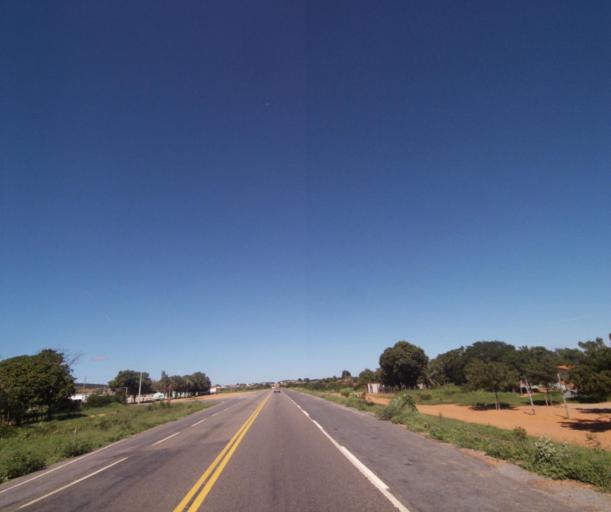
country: BR
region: Bahia
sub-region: Palmas De Monte Alto
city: Palmas de Monte Alto
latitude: -14.2490
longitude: -43.1560
